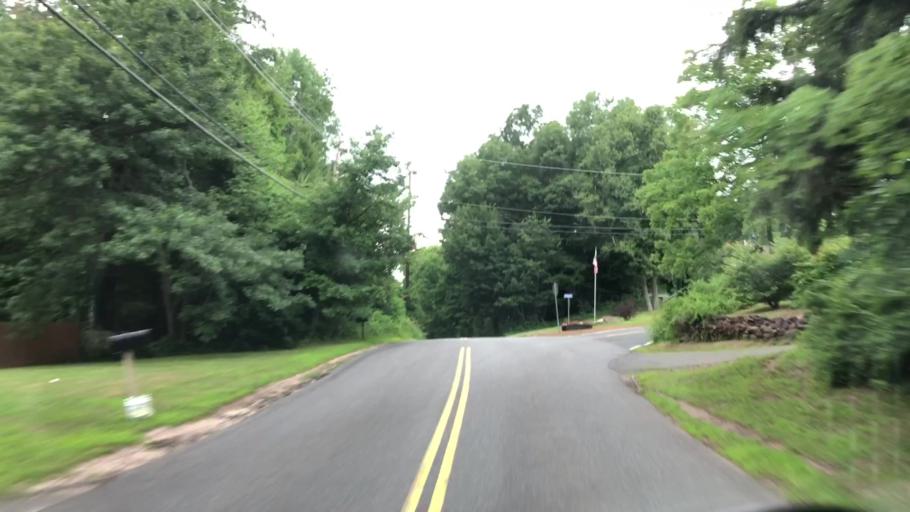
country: US
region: Massachusetts
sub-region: Hampden County
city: Holyoke
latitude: 42.1936
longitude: -72.6749
